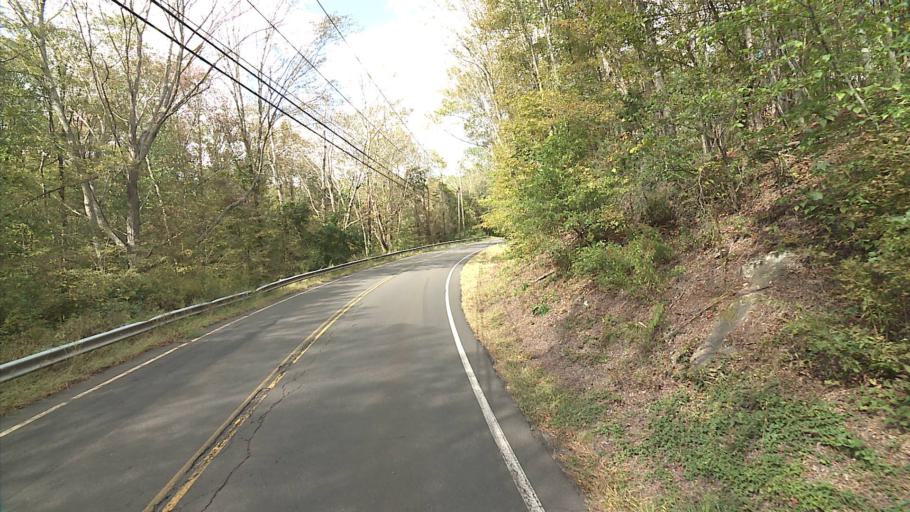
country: US
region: Connecticut
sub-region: Middlesex County
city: Durham
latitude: 41.4330
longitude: -72.6433
